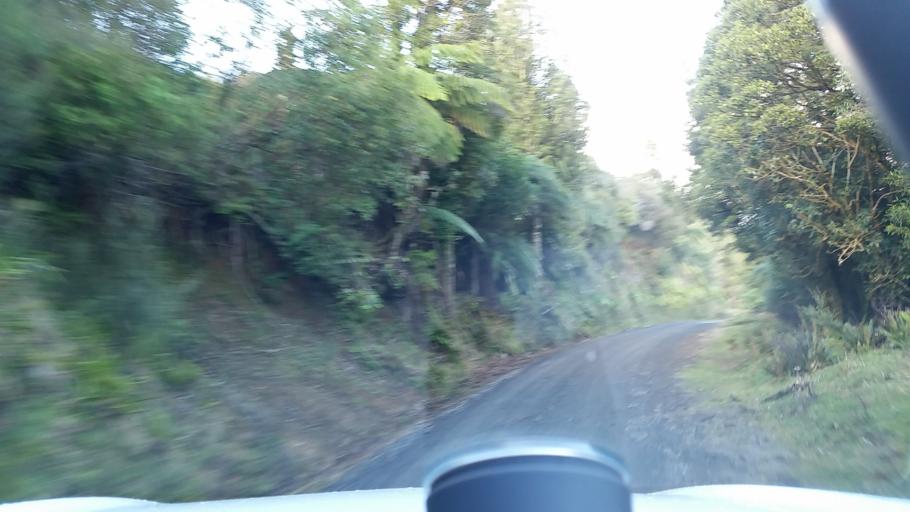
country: NZ
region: Taranaki
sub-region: South Taranaki District
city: Eltham
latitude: -39.4243
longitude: 174.5578
